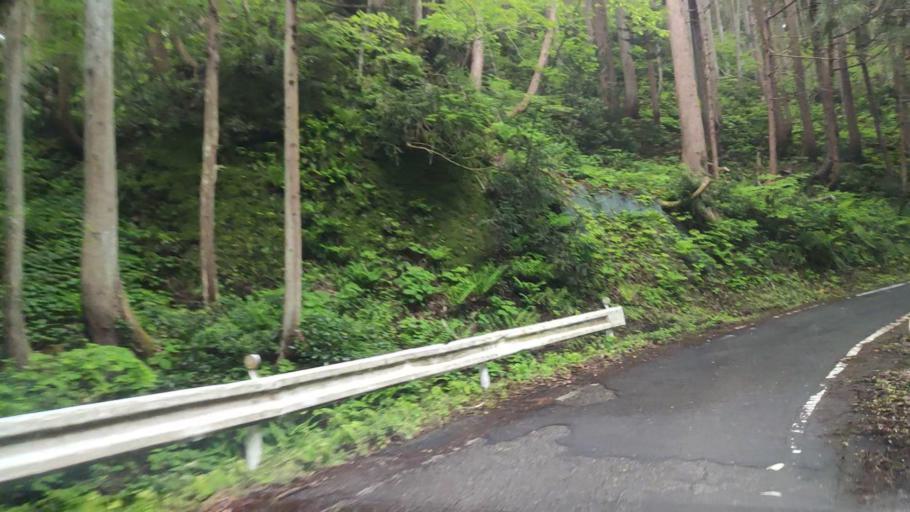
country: JP
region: Niigata
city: Kamo
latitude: 37.7173
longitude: 139.0907
